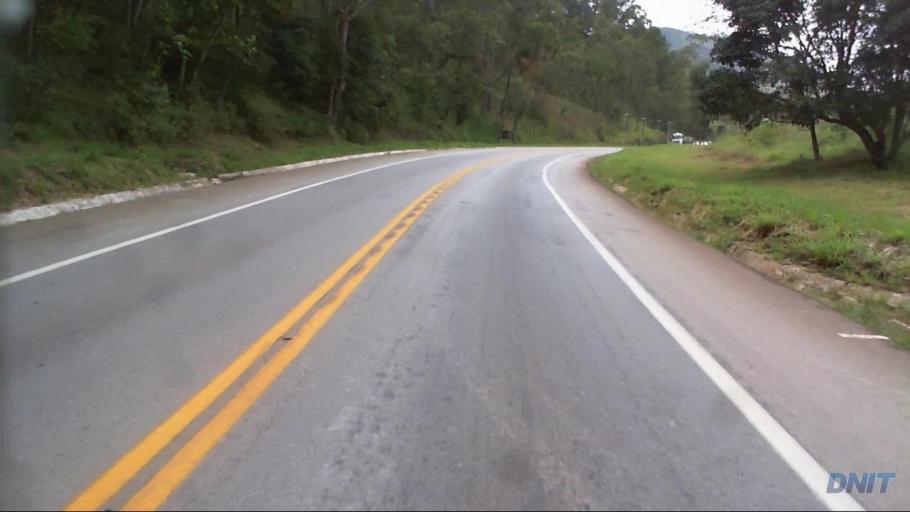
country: BR
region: Minas Gerais
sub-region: Joao Monlevade
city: Joao Monlevade
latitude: -19.8498
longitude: -43.1487
